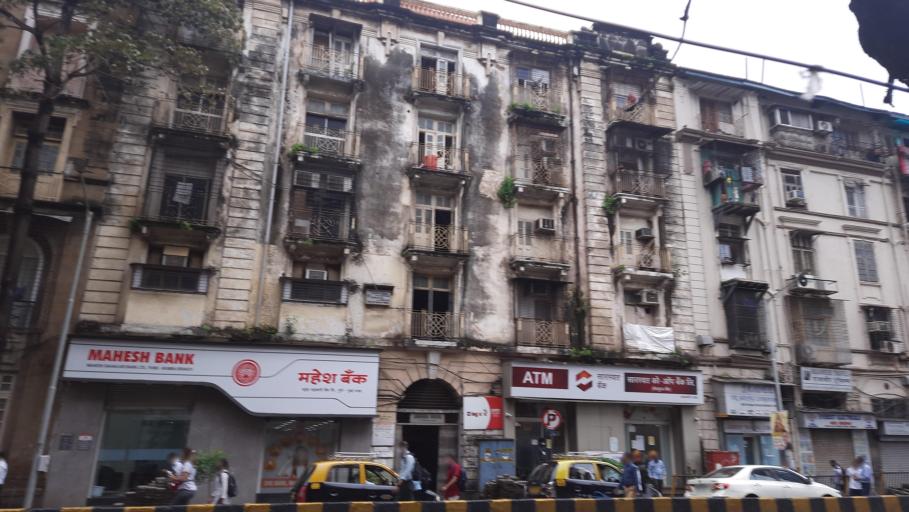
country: IN
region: Maharashtra
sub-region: Raigarh
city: Uran
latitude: 18.9451
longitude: 72.8262
